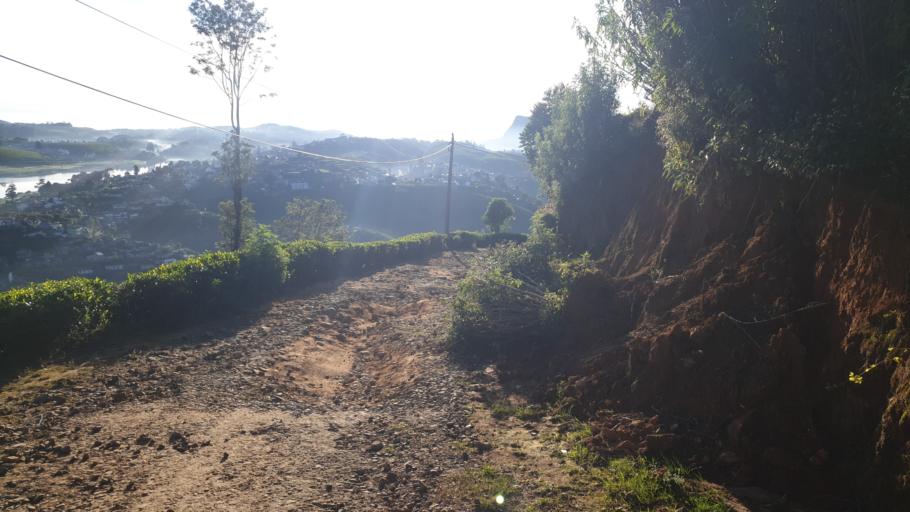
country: LK
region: Central
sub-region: Nuwara Eliya District
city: Nuwara Eliya
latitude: 6.9571
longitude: 80.7648
